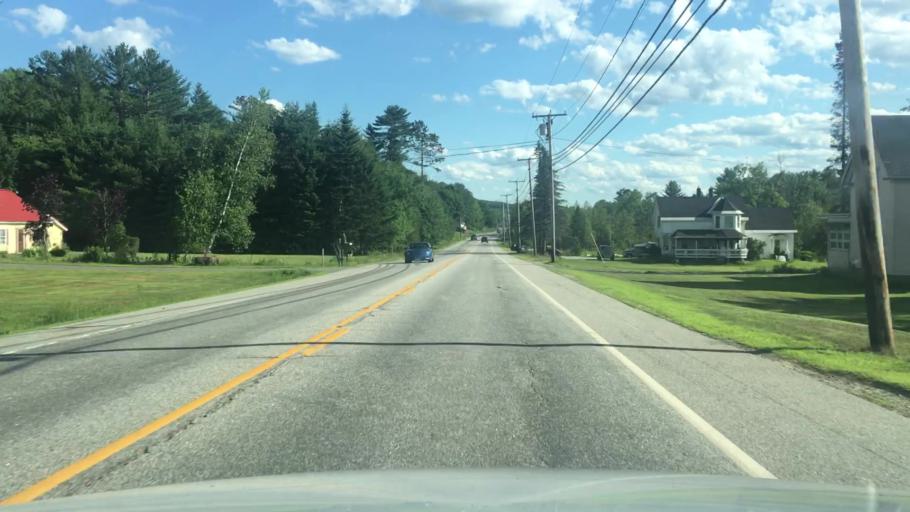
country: US
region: Maine
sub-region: Franklin County
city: Wilton
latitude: 44.5552
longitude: -70.2364
